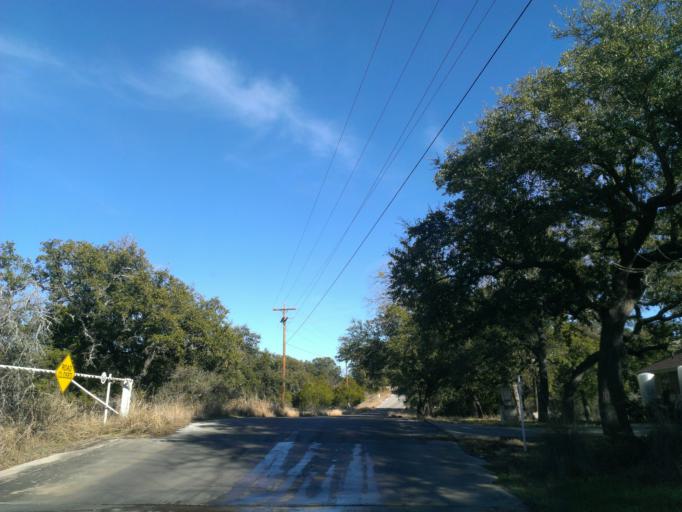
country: US
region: Texas
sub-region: Llano County
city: Horseshoe Bay
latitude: 30.5343
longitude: -98.3300
